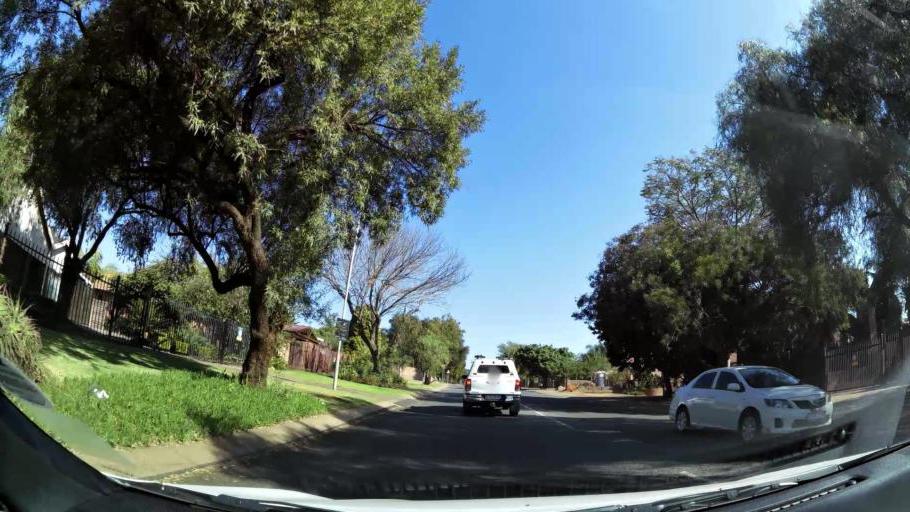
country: ZA
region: Gauteng
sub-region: City of Tshwane Metropolitan Municipality
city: Pretoria
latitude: -25.7902
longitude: 28.2736
